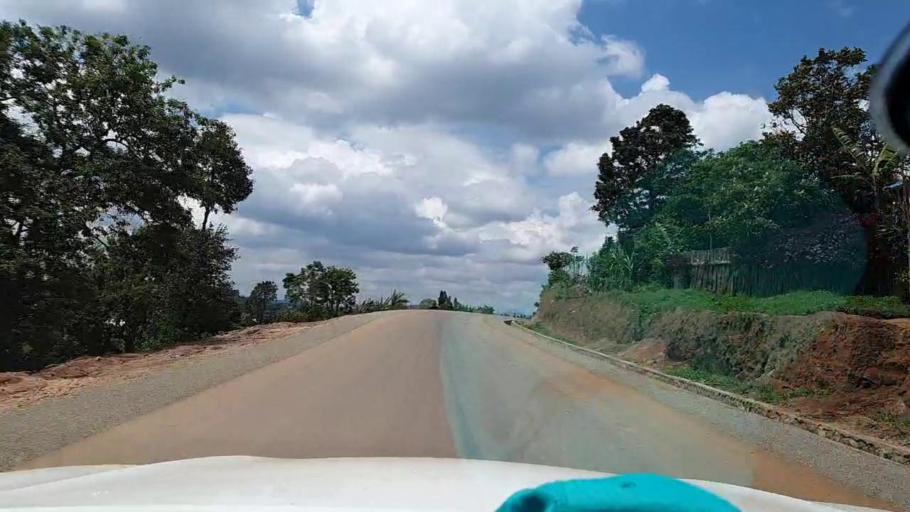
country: RW
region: Southern Province
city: Nzega
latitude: -2.6466
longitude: 29.5689
